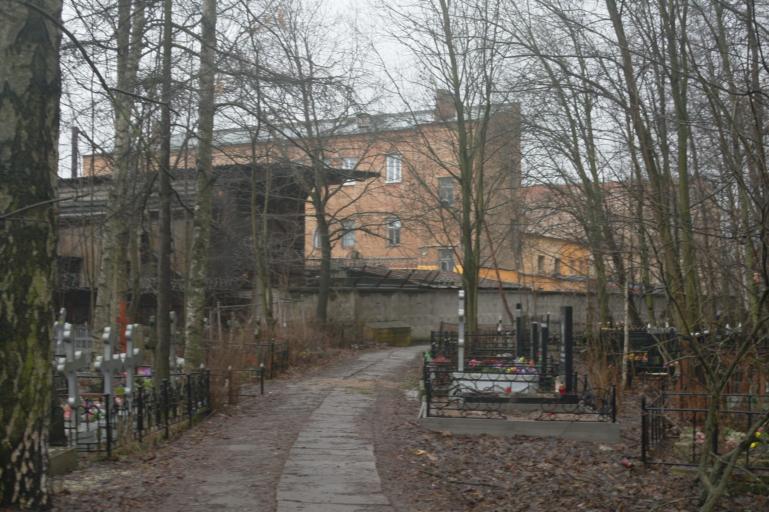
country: RU
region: St.-Petersburg
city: Komendantsky aerodrom
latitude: 59.9909
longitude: 30.2725
